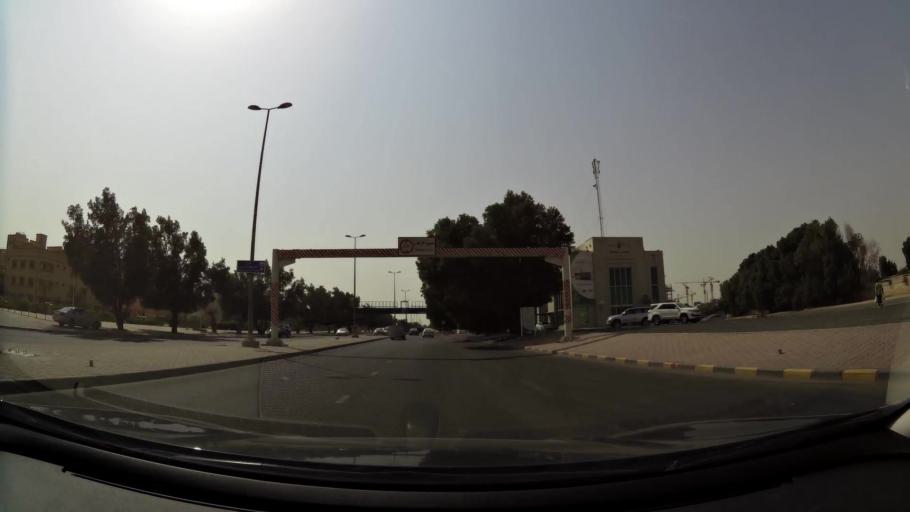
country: KW
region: Muhafazat al Jahra'
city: Al Jahra'
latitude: 29.3406
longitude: 47.6895
